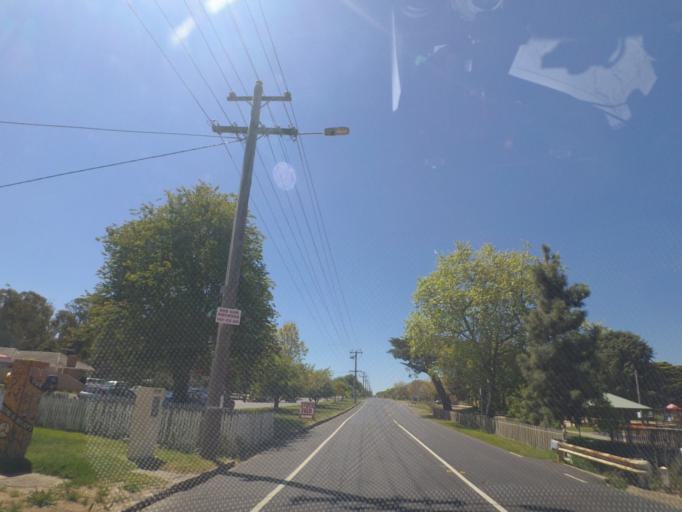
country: AU
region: Victoria
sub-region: Hume
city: Sunbury
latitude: -37.4625
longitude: 144.6769
